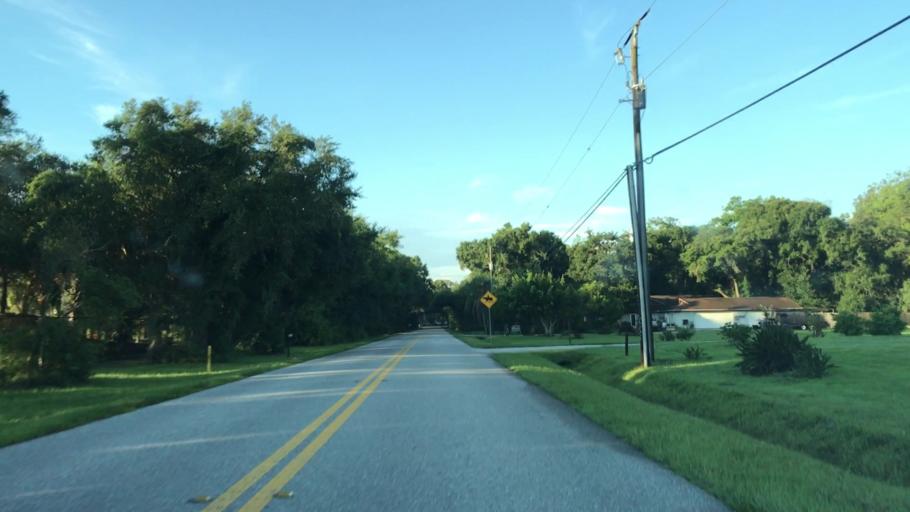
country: US
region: Florida
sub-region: Sarasota County
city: Fruitville
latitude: 27.3370
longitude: -82.4051
